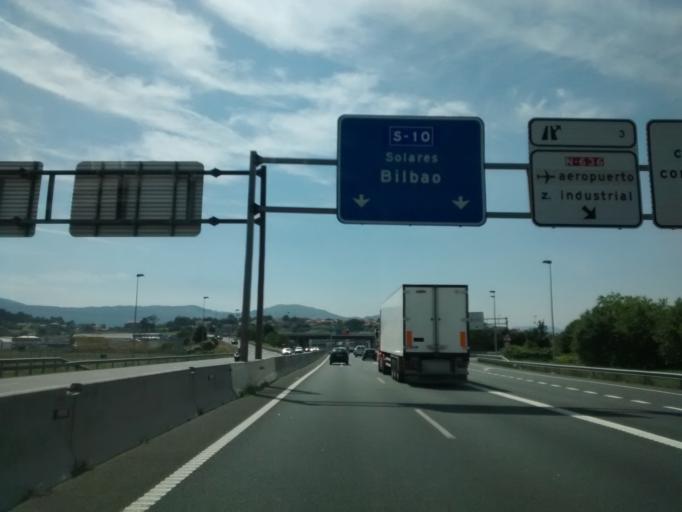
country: ES
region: Cantabria
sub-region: Provincia de Cantabria
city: El Astillero
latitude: 43.4289
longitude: -3.8363
